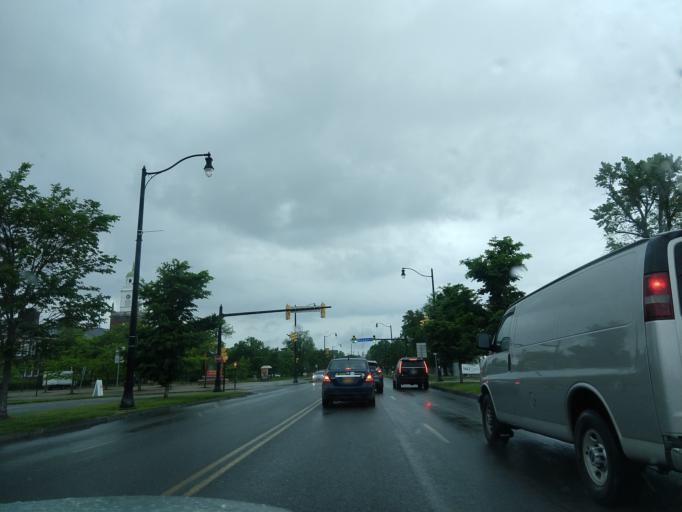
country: US
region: New York
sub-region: Erie County
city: Kenmore
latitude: 42.9314
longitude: -78.8770
